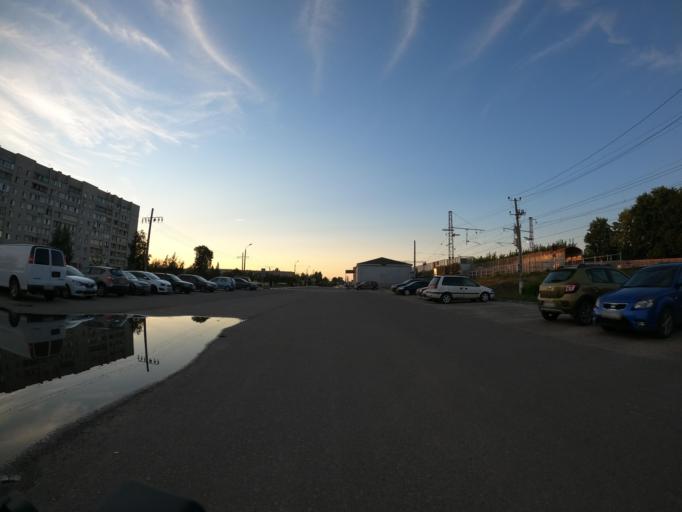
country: RU
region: Moskovskaya
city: Kolomna
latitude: 55.0982
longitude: 38.7811
